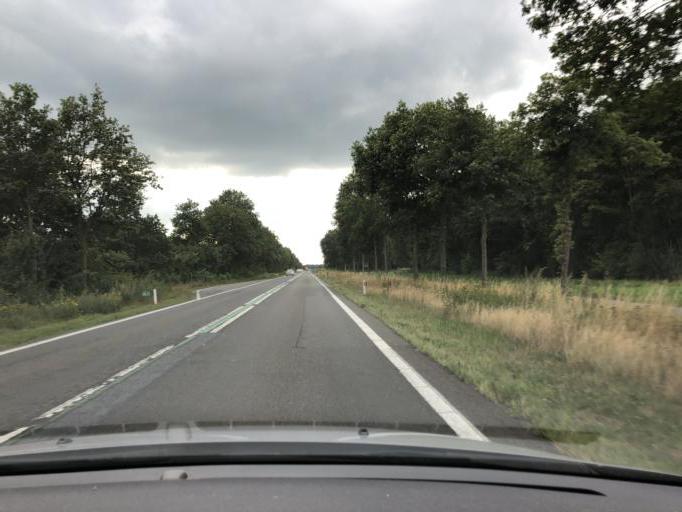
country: NL
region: Drenthe
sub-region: Gemeente Hoogeveen
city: Hoogeveen
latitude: 52.6127
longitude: 6.5001
